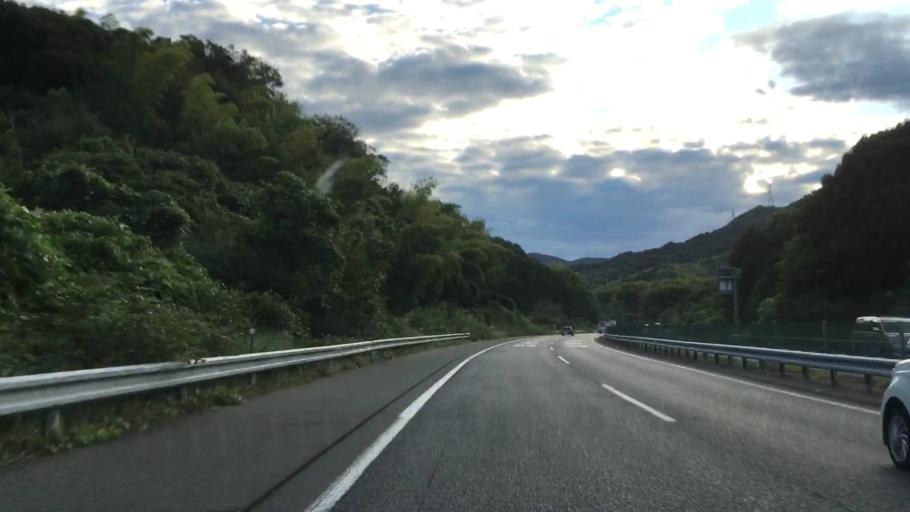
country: JP
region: Yamaguchi
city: Shimonoseki
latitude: 34.0452
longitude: 130.9954
